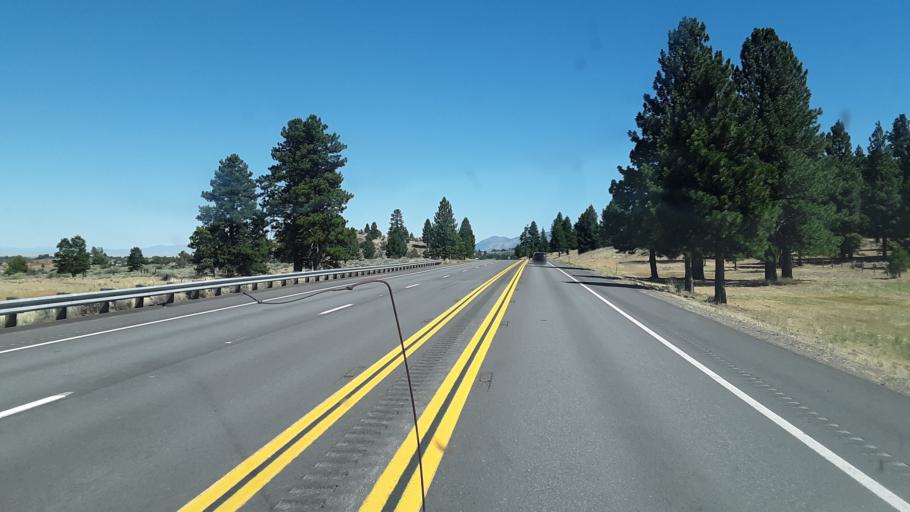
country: US
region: California
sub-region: Lassen County
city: Janesville
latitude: 40.3075
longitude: -120.5306
